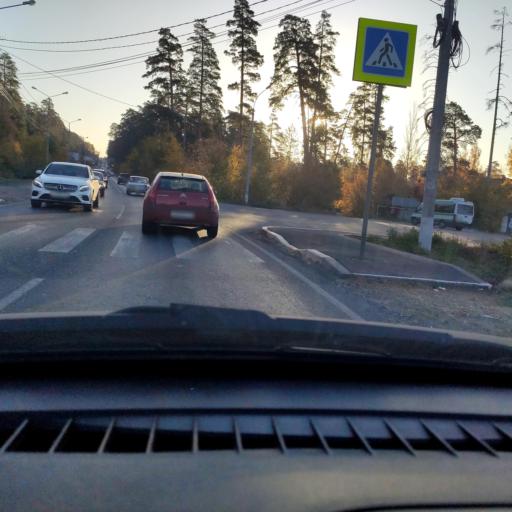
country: RU
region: Samara
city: Tol'yatti
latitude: 53.4764
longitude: 49.3264
